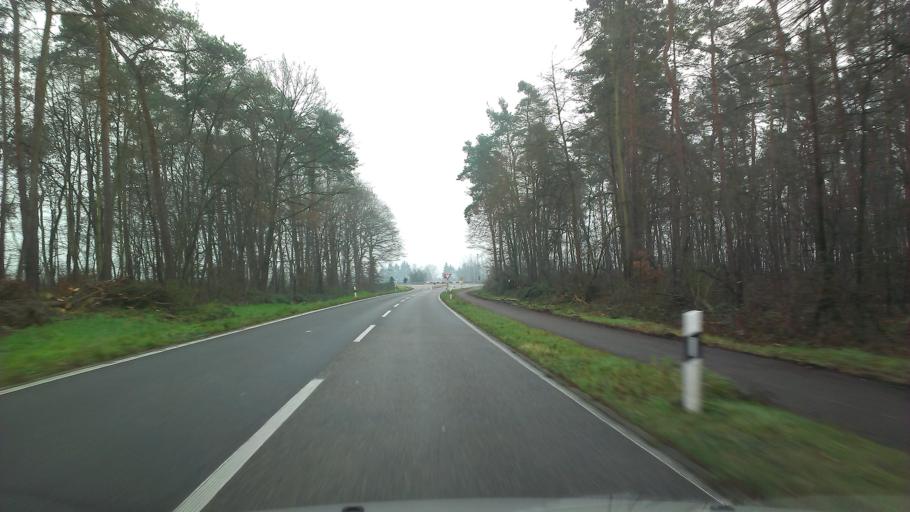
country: DE
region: Baden-Wuerttemberg
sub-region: Karlsruhe Region
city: Forst
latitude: 49.1719
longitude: 8.6016
